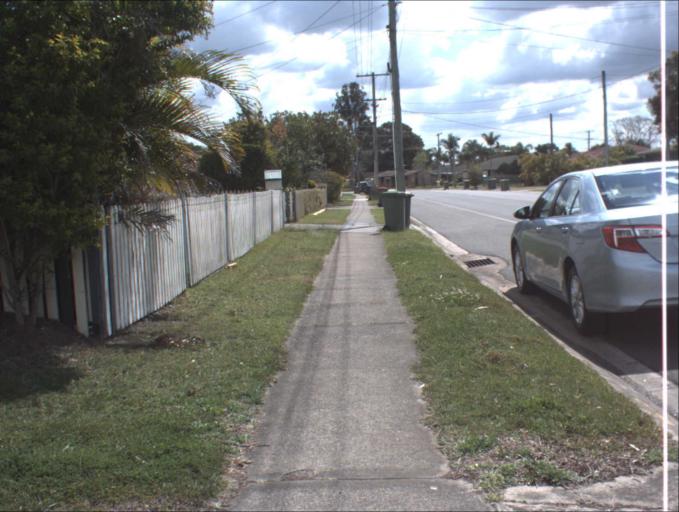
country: AU
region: Queensland
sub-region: Logan
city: Waterford West
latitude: -27.6844
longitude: 153.1532
